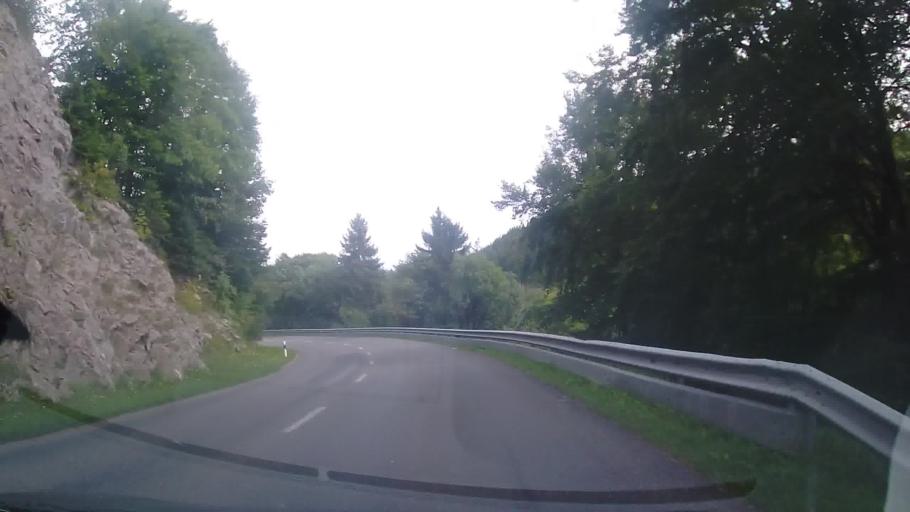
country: CH
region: Vaud
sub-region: Nyon District
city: Saint-Cergue
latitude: 46.4474
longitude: 6.1443
